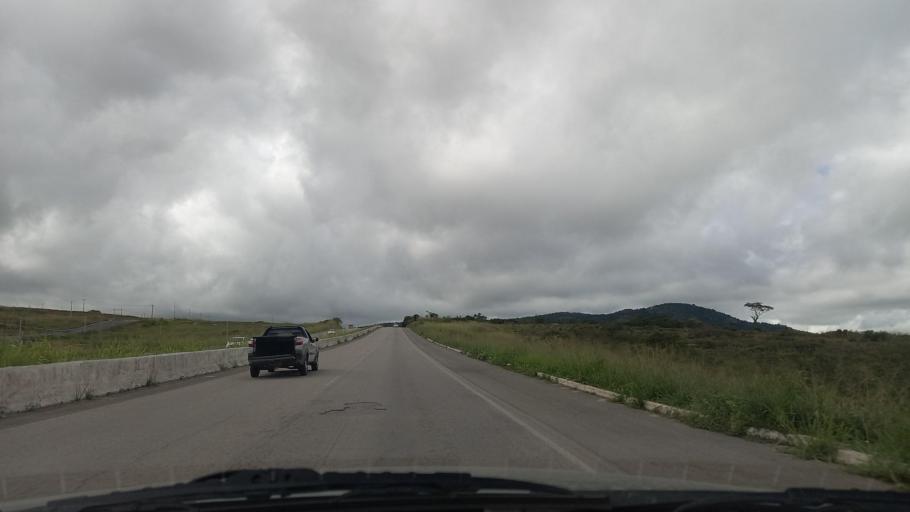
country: BR
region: Pernambuco
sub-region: Caruaru
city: Caruaru
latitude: -8.3235
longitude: -35.9890
